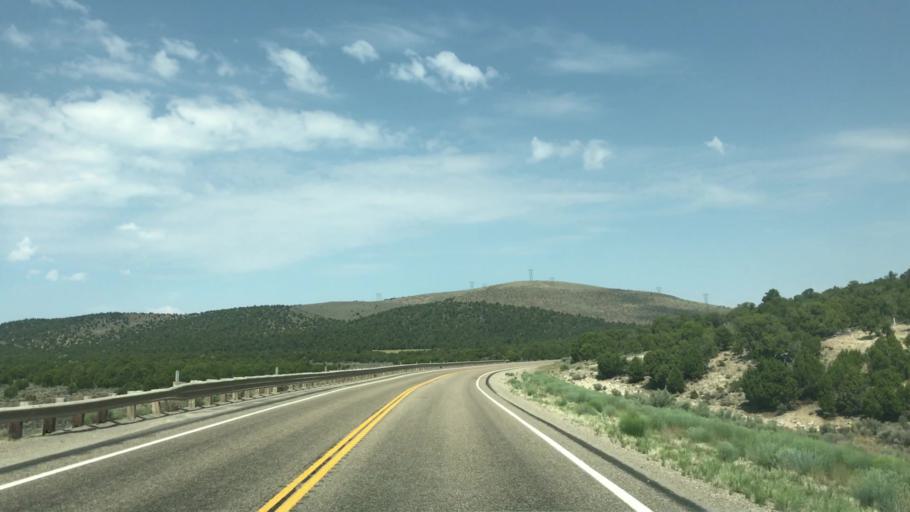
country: US
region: Nevada
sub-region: White Pine County
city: Ely
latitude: 39.3911
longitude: -115.0802
